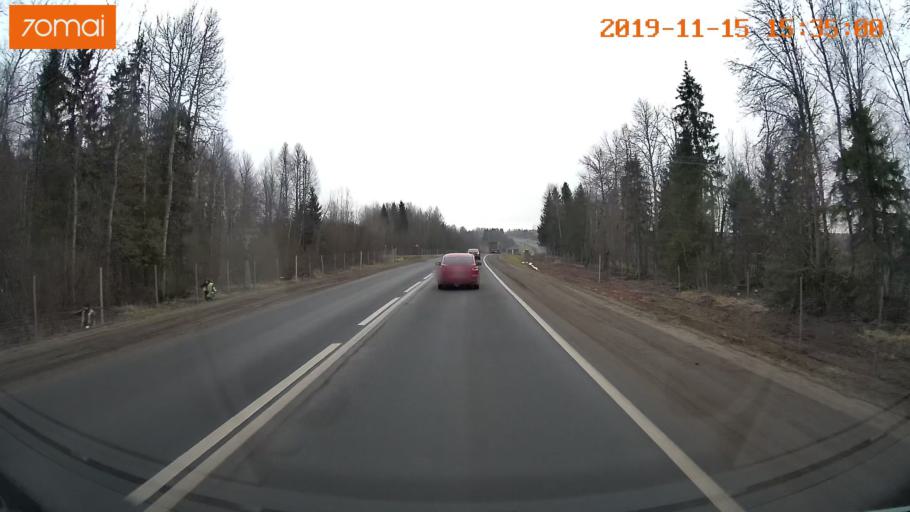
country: RU
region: Jaroslavl
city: Danilov
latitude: 58.0638
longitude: 40.0883
